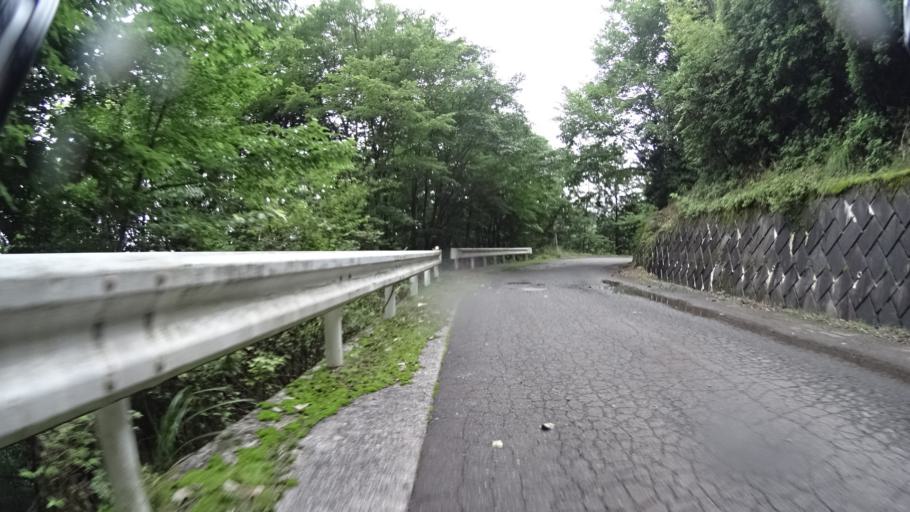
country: JP
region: Saitama
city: Chichibu
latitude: 35.8861
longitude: 139.1192
